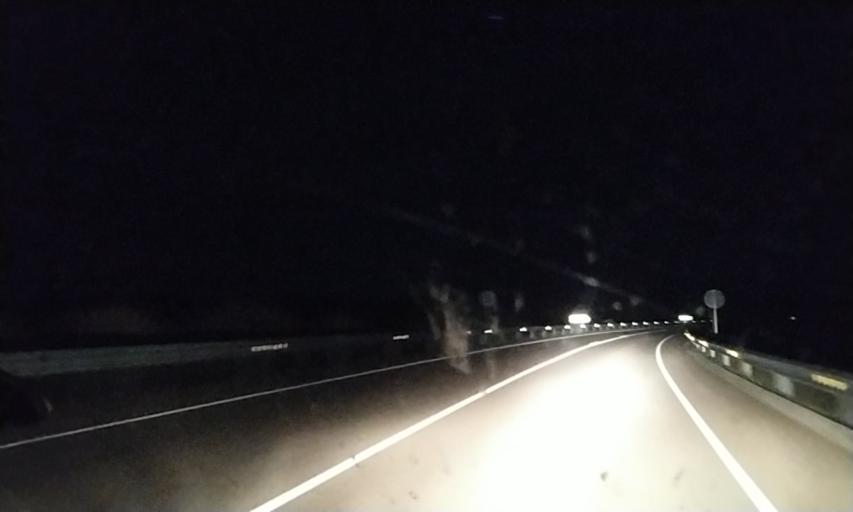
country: ES
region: Castille and Leon
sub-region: Provincia de Salamanca
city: Herguijuela de Ciudad Rodrigo
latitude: 40.4859
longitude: -6.5823
